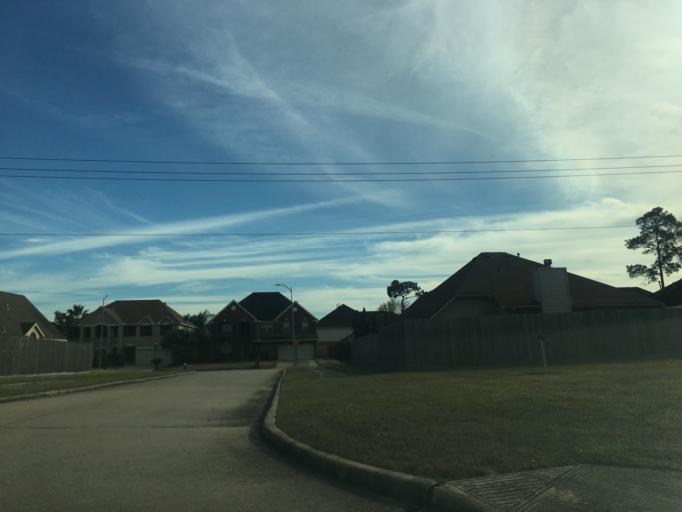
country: US
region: Texas
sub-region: Harris County
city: Cloverleaf
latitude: 29.8161
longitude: -95.1698
